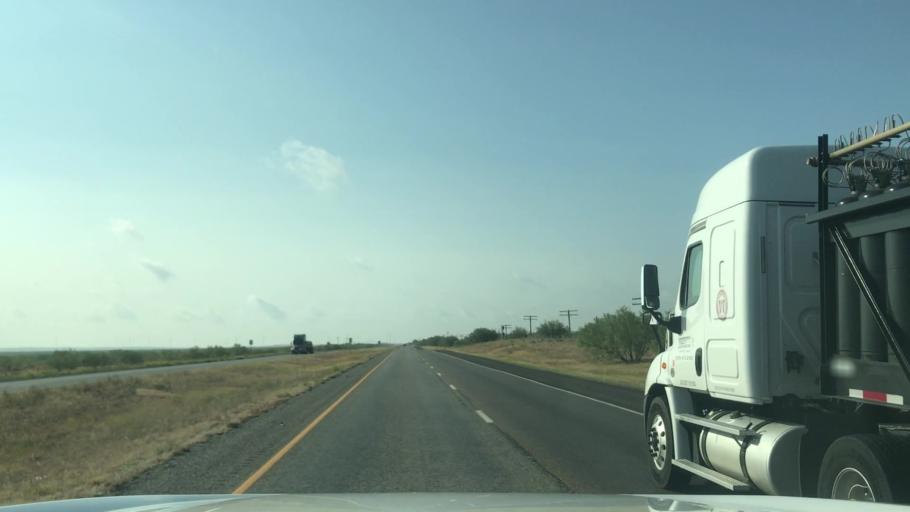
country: US
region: Texas
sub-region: Scurry County
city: Snyder
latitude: 32.9653
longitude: -101.0948
